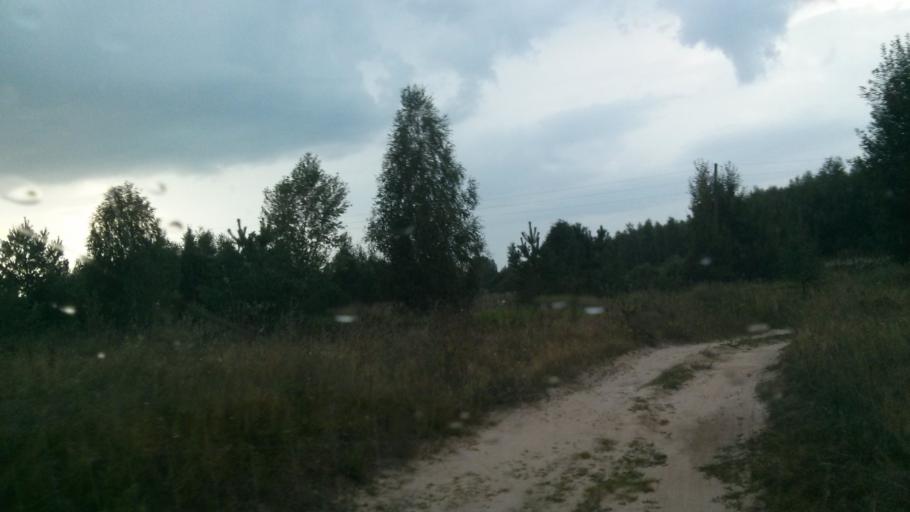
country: RU
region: Nizjnij Novgorod
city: Shimorskoye
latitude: 55.3147
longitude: 41.8619
